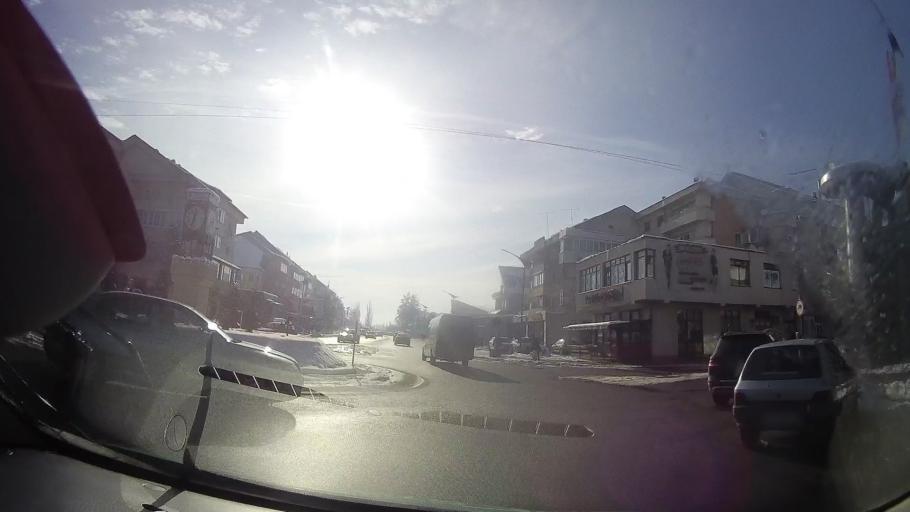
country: RO
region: Neamt
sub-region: Oras Targu Neamt
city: Humulesti
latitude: 47.2048
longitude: 26.3589
